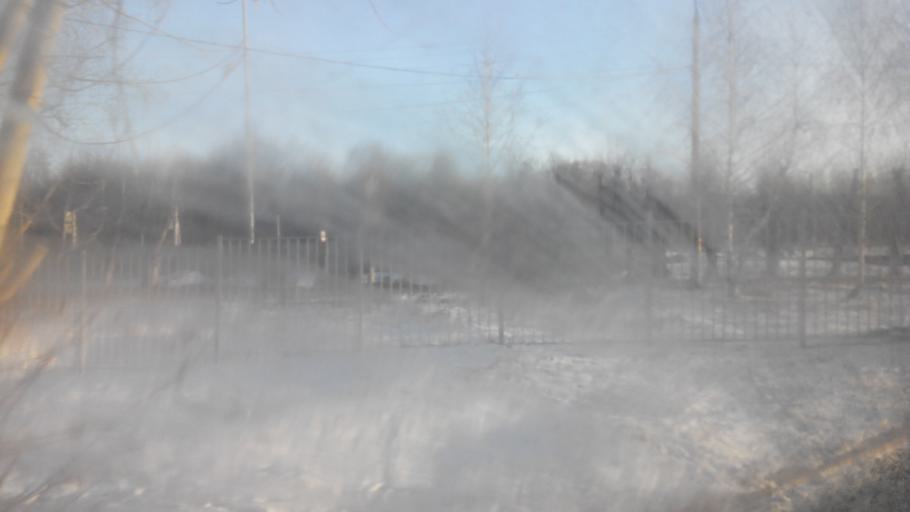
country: RU
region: Tula
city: Uzlovaya
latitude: 53.9727
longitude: 38.1758
